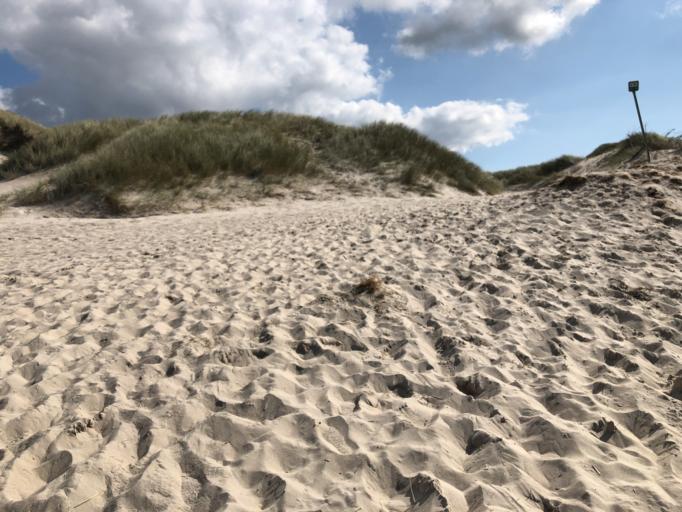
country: DK
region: Central Jutland
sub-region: Ringkobing-Skjern Kommune
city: Ringkobing
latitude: 56.1769
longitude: 8.1219
